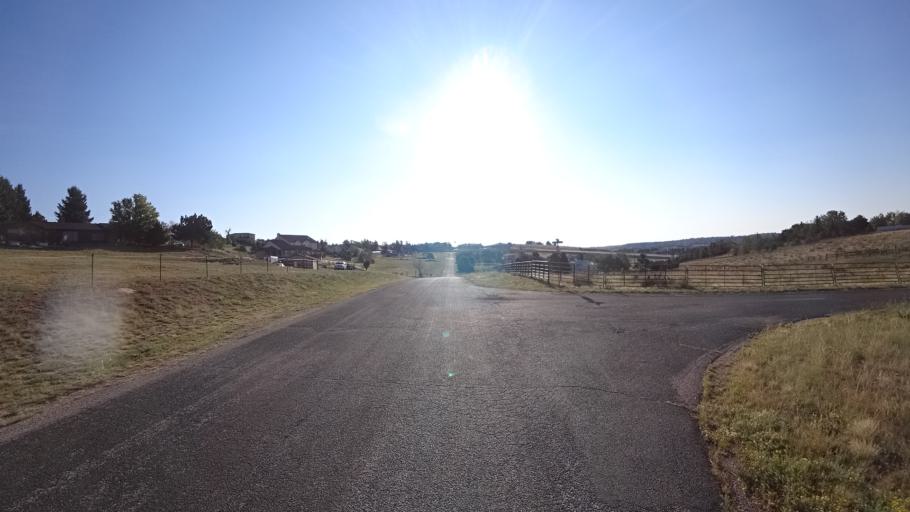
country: US
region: Colorado
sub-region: El Paso County
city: Black Forest
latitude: 38.9367
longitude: -104.7724
